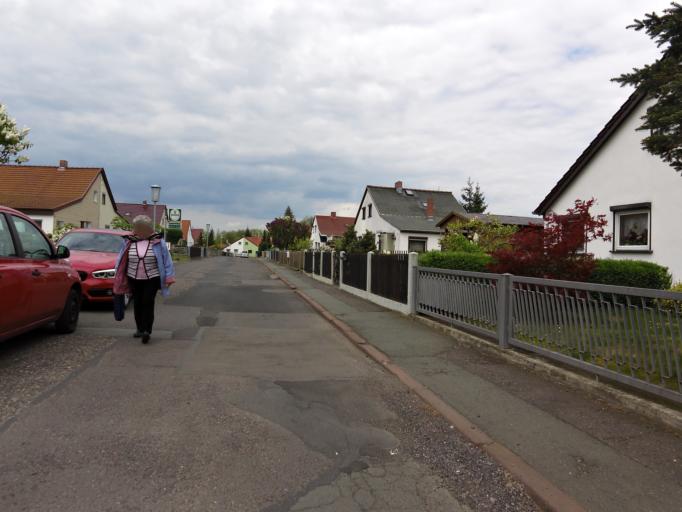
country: DE
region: Thuringia
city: Gotha
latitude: 50.9307
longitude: 10.7123
